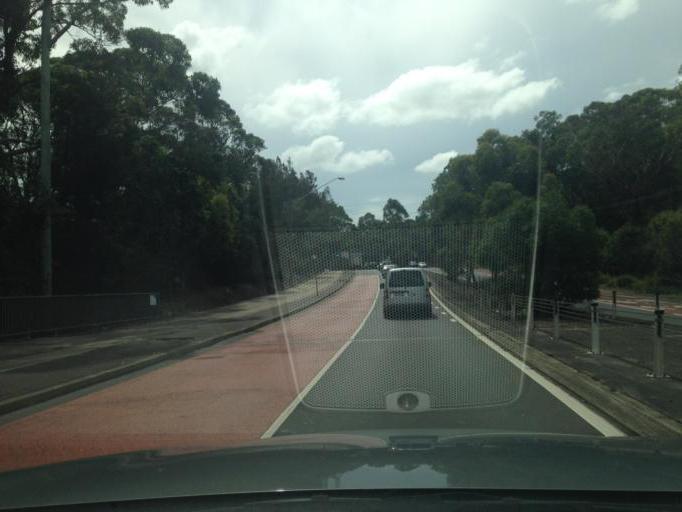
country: AU
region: New South Wales
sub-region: Lane Cove
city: Lane Cove West
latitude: -33.8081
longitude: 151.1547
